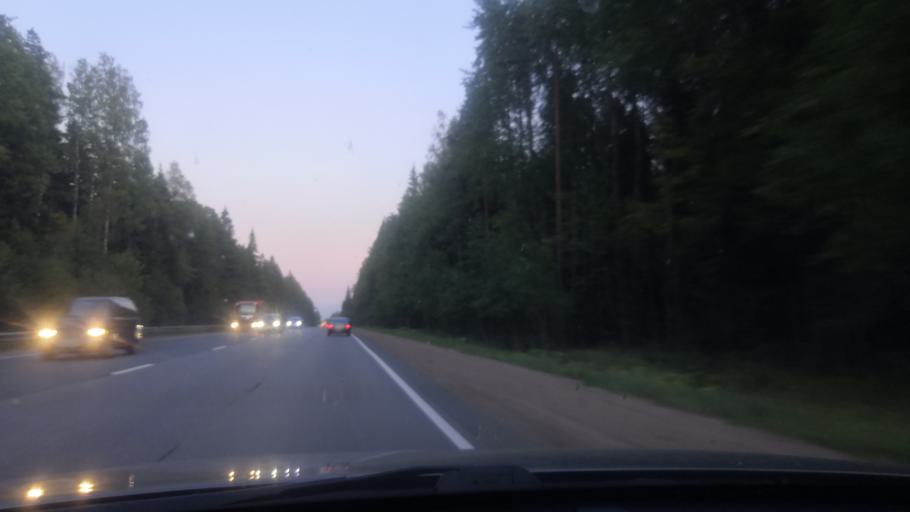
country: RU
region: St.-Petersburg
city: Pesochnyy
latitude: 60.1849
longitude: 30.1172
